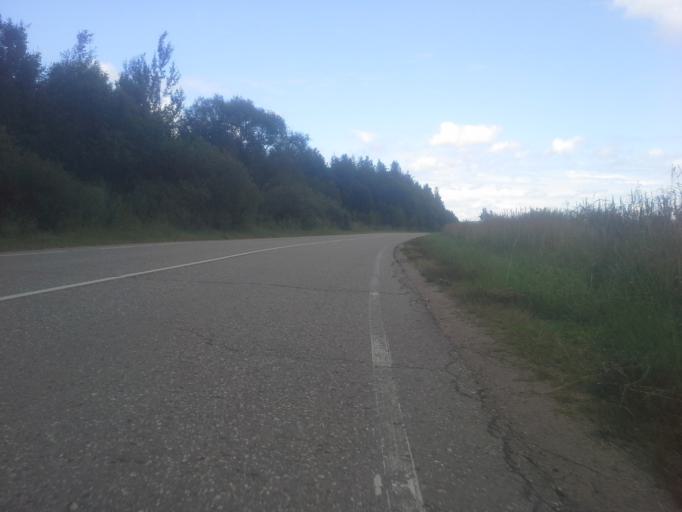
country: RU
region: Moskovskaya
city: Kolyubakino
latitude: 55.6477
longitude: 36.5735
